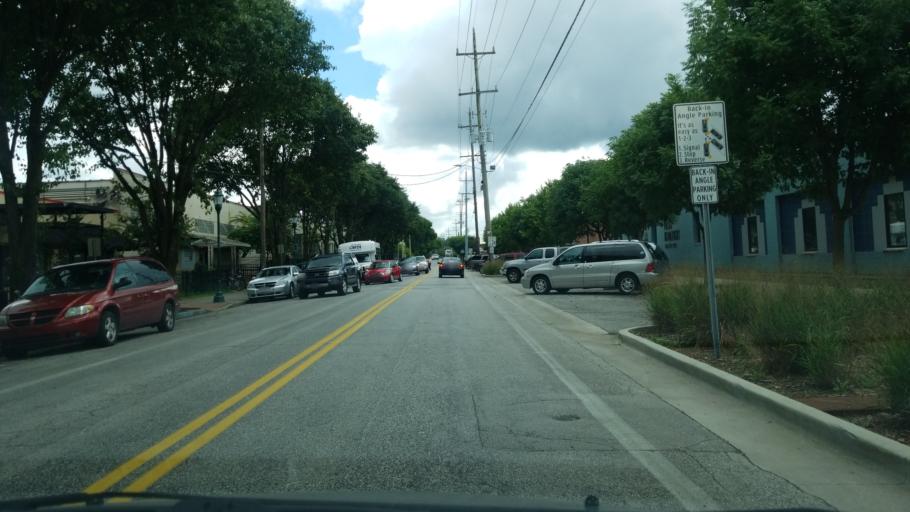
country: US
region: Tennessee
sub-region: Hamilton County
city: Chattanooga
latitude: 35.0406
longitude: -85.3007
